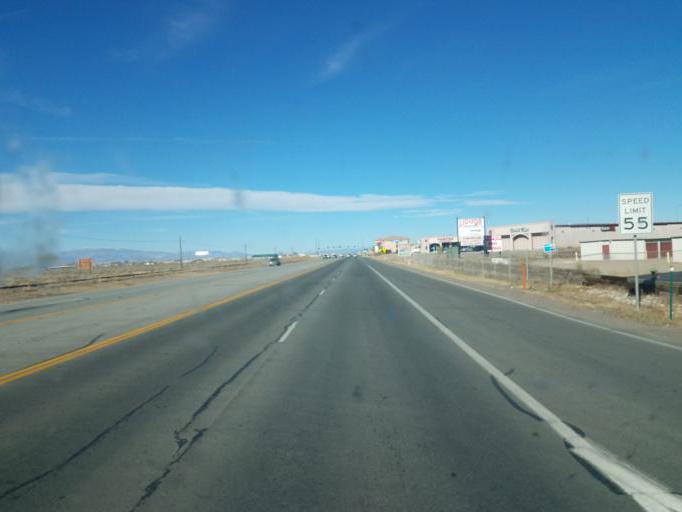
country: US
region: Colorado
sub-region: Alamosa County
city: Alamosa
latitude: 37.4788
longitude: -105.9030
